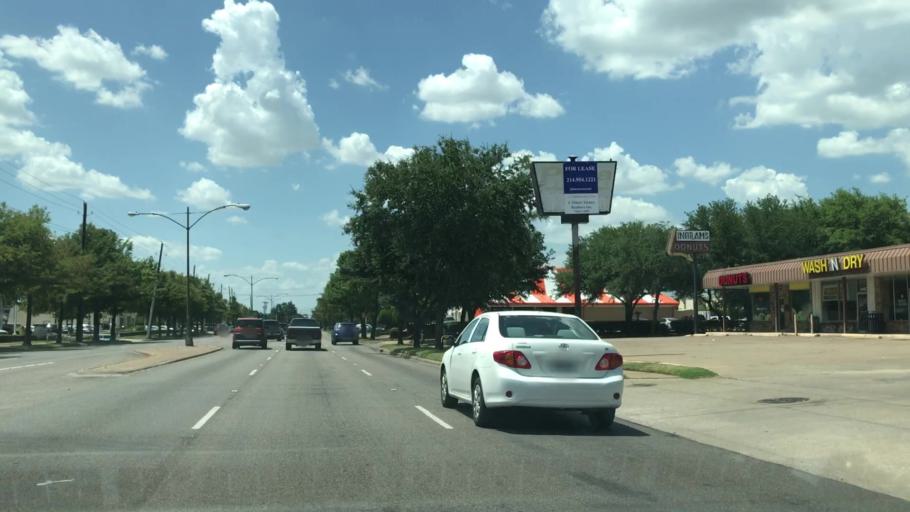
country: US
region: Texas
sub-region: Dallas County
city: Highland Park
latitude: 32.8279
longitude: -96.8239
